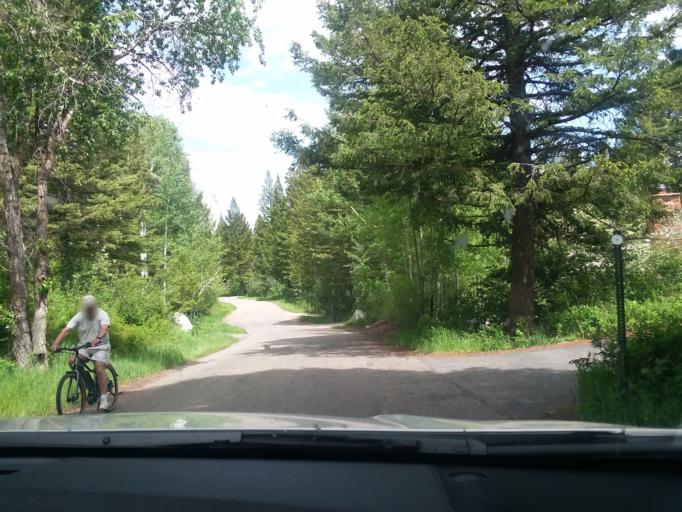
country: US
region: Wyoming
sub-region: Teton County
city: Moose Wilson Road
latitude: 43.5869
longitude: -110.8381
